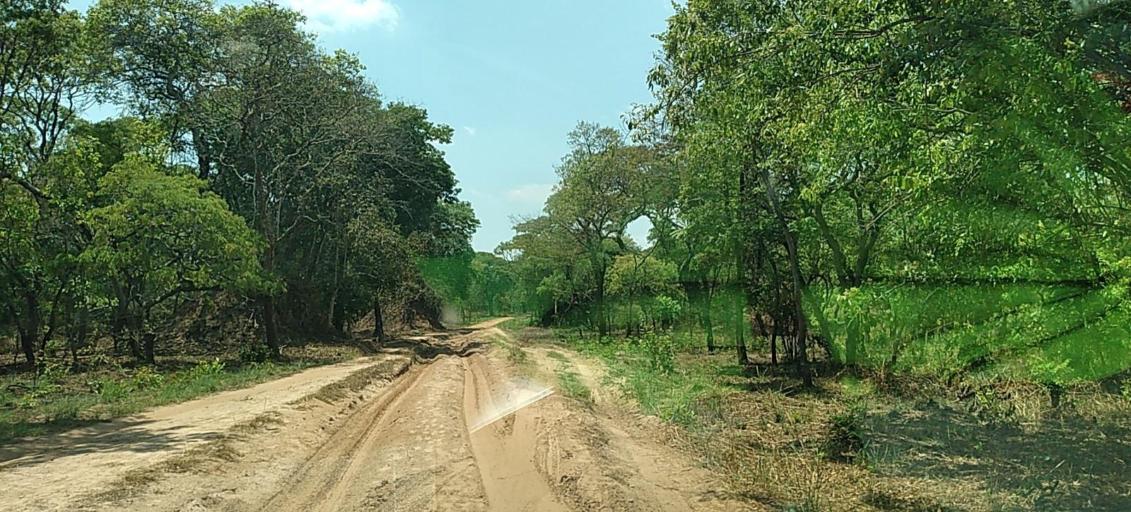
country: CD
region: Katanga
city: Kolwezi
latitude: -11.3611
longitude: 25.2060
